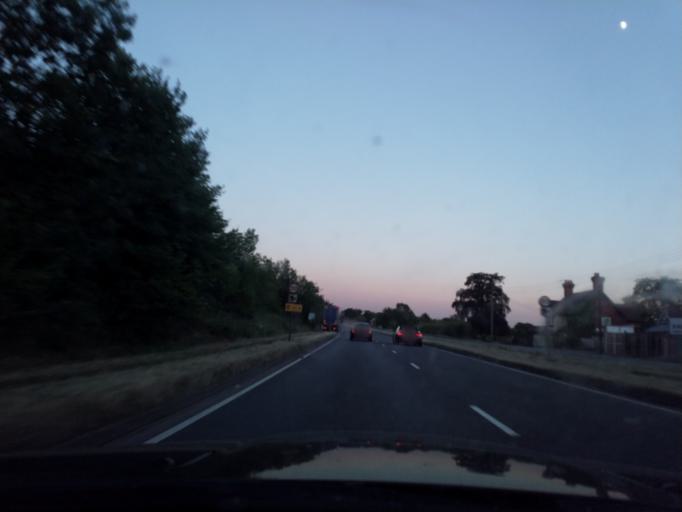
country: GB
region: England
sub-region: Solihull
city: Barston
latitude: 52.4172
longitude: -1.6764
